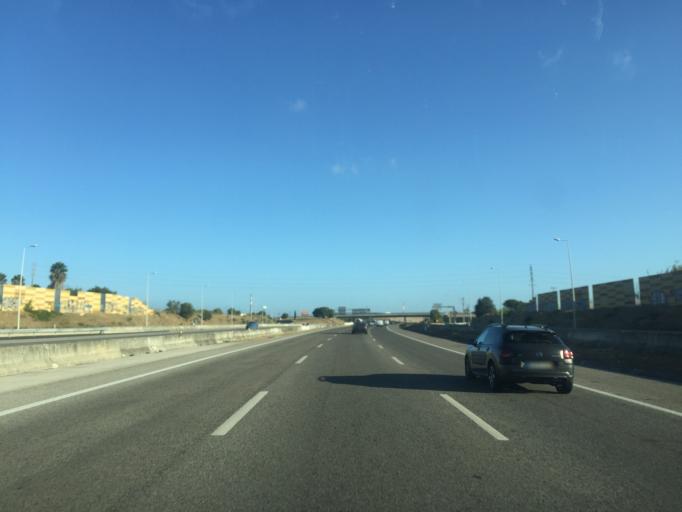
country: PT
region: Lisbon
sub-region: Alenquer
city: Carregado
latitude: 39.0204
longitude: -8.9652
